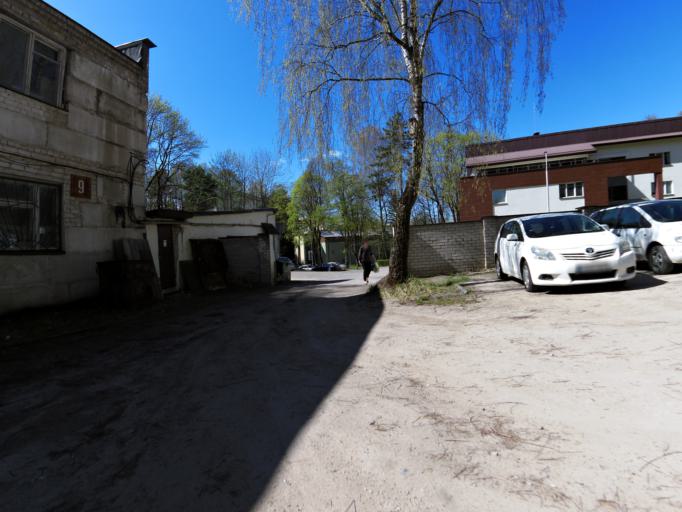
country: LT
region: Vilnius County
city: Rasos
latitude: 54.6900
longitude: 25.3091
